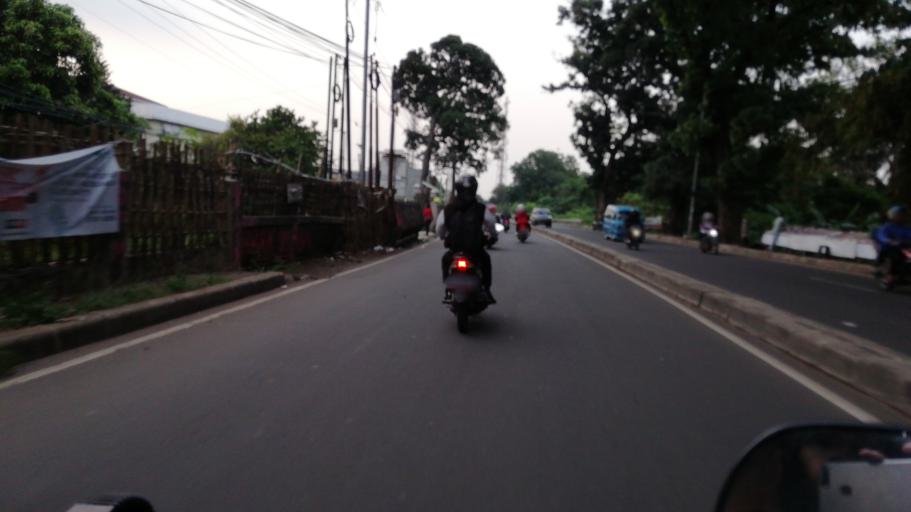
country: ID
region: West Java
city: Cibinong
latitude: -6.4403
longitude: 106.8529
